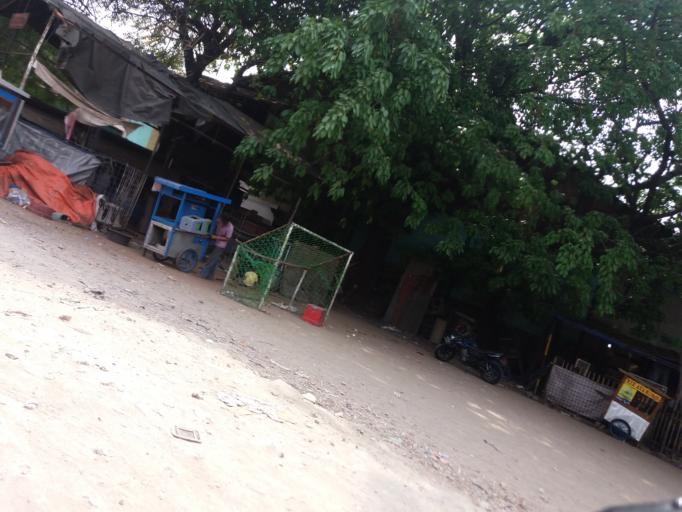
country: ID
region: Jakarta Raya
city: Jakarta
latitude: -6.1308
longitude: 106.8137
